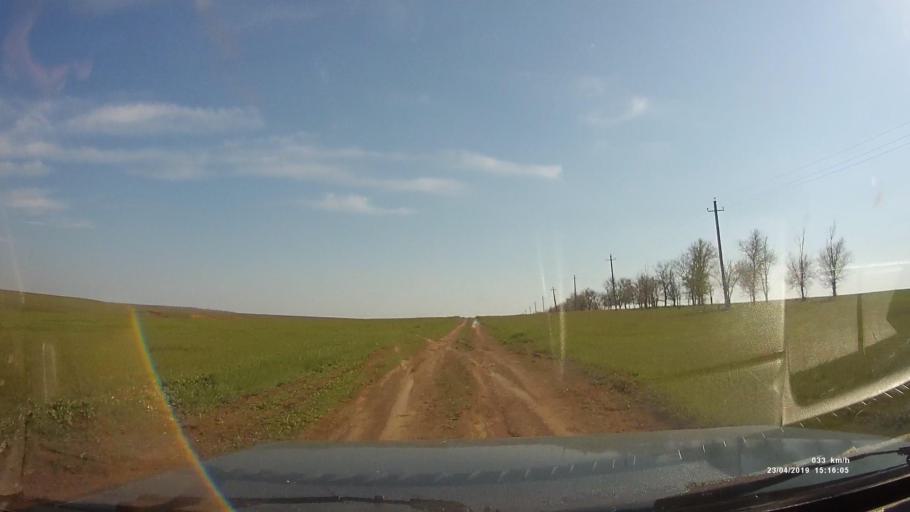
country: RU
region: Rostov
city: Remontnoye
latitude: 46.5358
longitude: 42.9697
